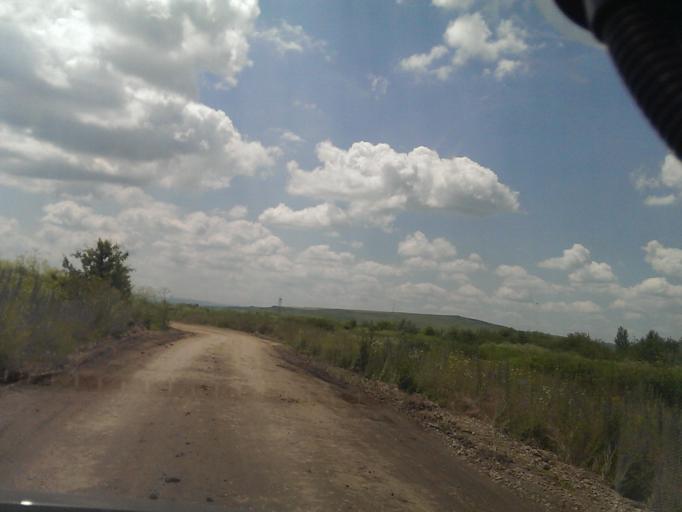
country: RO
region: Cluj
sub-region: Comuna Bontida
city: Rascruci
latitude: 46.9149
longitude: 23.8027
